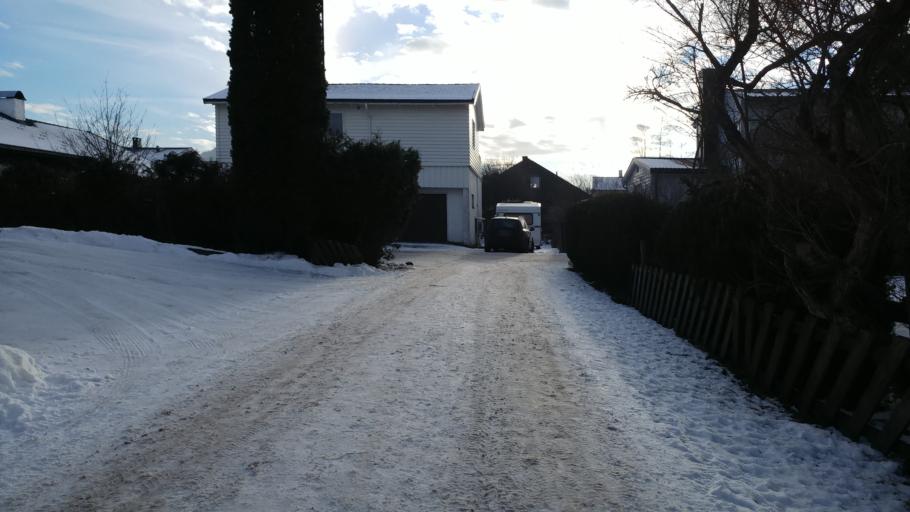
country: NO
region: Akershus
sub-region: Skedsmo
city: Lillestrom
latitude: 59.9564
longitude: 11.0413
